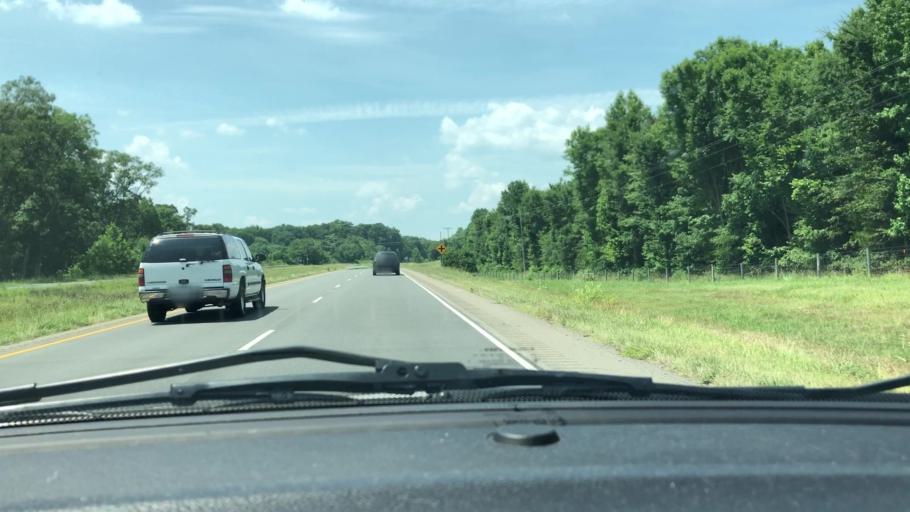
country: US
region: North Carolina
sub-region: Chatham County
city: Siler City
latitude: 35.6645
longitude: -79.4055
